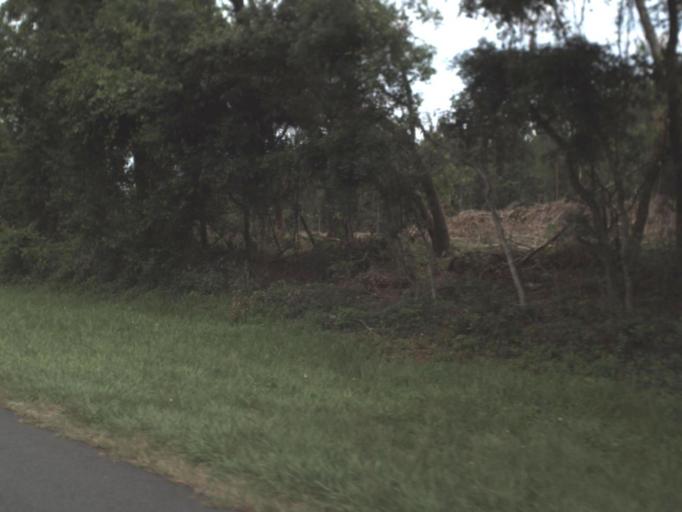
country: US
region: Florida
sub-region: Alachua County
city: Hawthorne
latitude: 29.5957
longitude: -82.0532
